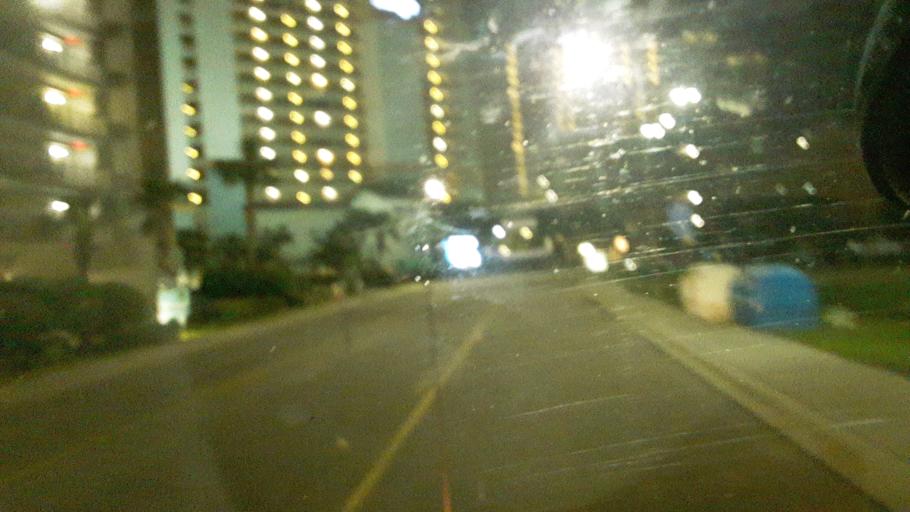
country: US
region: South Carolina
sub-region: Horry County
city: North Myrtle Beach
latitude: 33.7915
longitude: -78.7340
